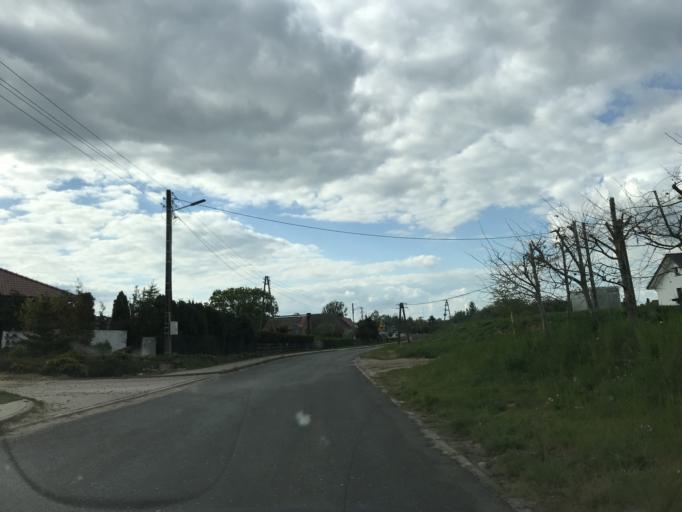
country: PL
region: West Pomeranian Voivodeship
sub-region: Powiat mysliborski
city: Mysliborz
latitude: 52.9173
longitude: 14.8868
